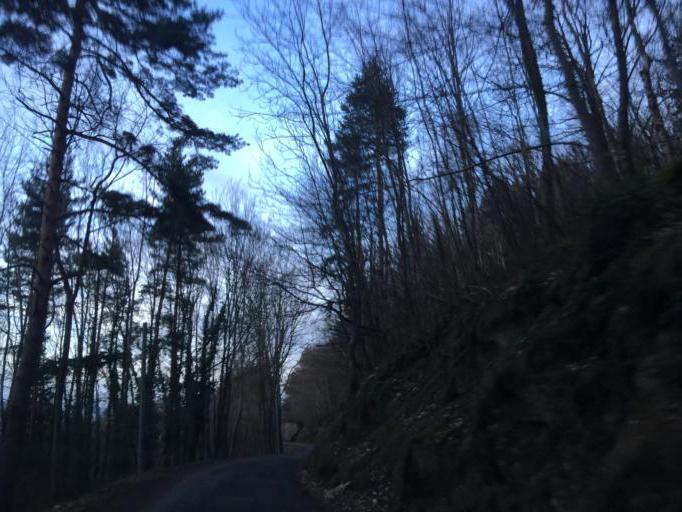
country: FR
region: Rhone-Alpes
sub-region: Departement de la Loire
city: Saint-Jean-Bonnefonds
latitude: 45.4291
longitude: 4.4807
